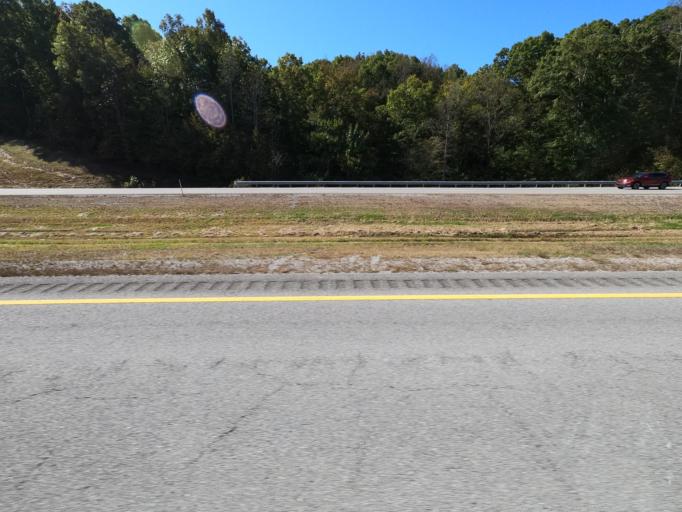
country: US
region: Tennessee
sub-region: Williamson County
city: Fairview
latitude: 35.8858
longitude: -87.1080
